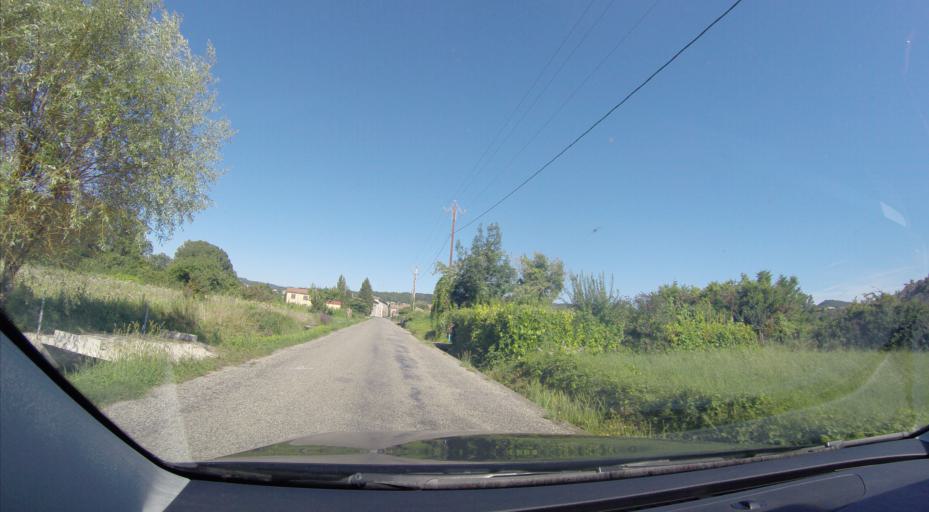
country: FR
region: Rhone-Alpes
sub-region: Departement de l'Ardeche
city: Saint-Privat
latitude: 44.6238
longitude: 4.4242
